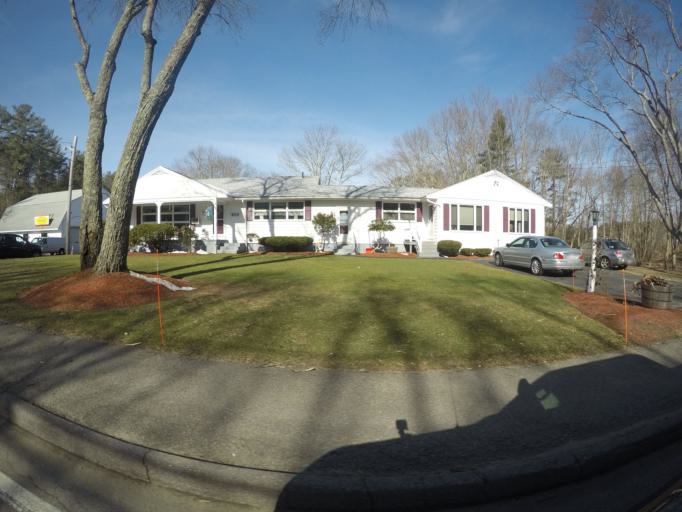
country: US
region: Massachusetts
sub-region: Bristol County
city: Easton
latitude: 42.0219
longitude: -71.1212
